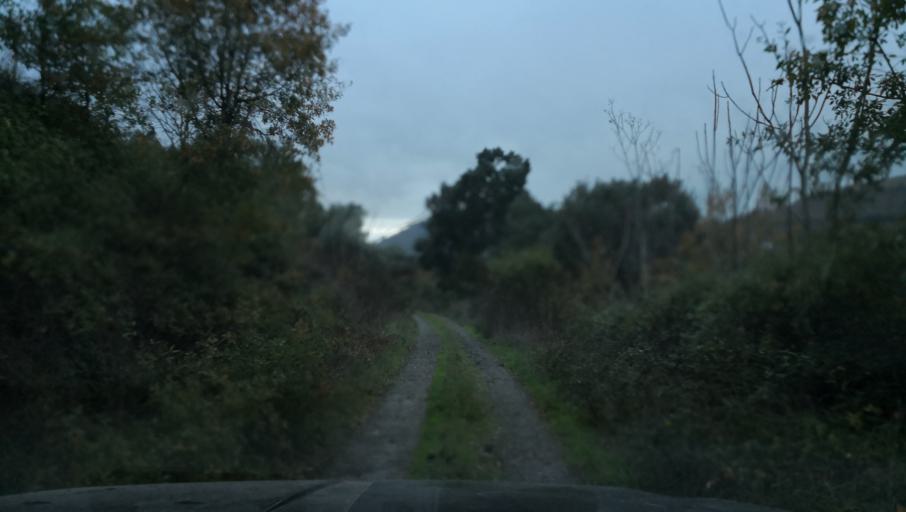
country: PT
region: Vila Real
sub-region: Santa Marta de Penaguiao
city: Santa Marta de Penaguiao
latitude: 41.2071
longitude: -7.7598
